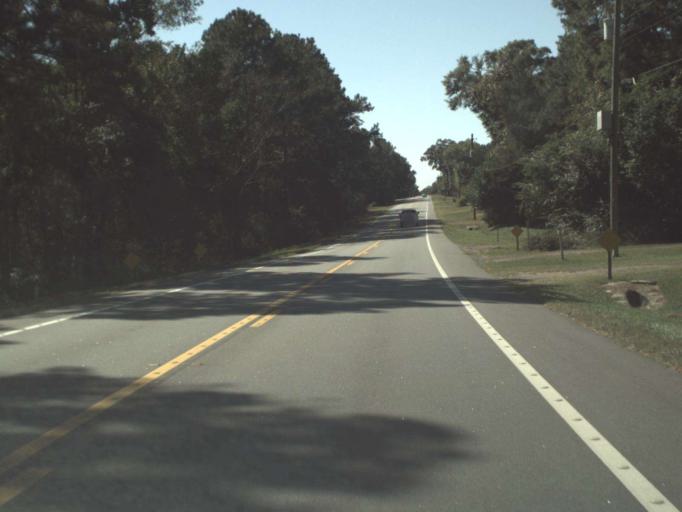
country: US
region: Alabama
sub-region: Covington County
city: Florala
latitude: 30.9812
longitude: -86.3439
